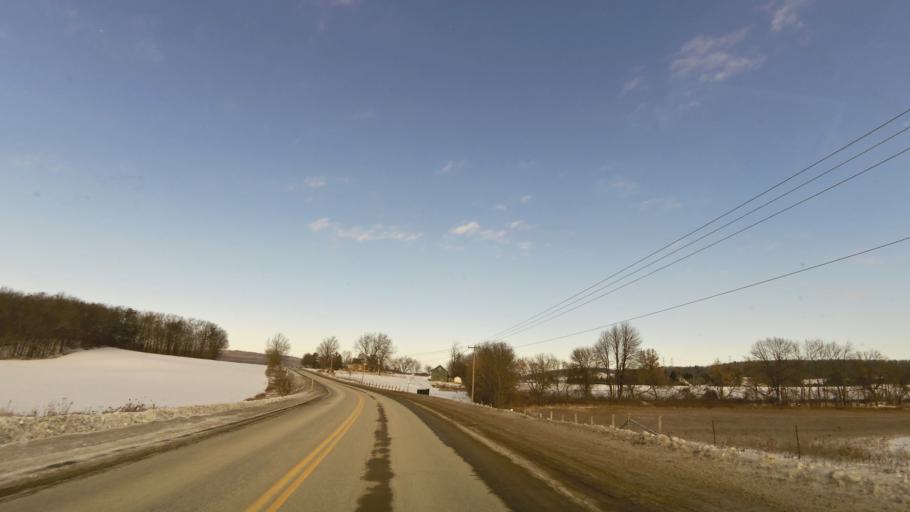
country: CA
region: Ontario
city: Quinte West
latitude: 44.1415
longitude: -77.7898
